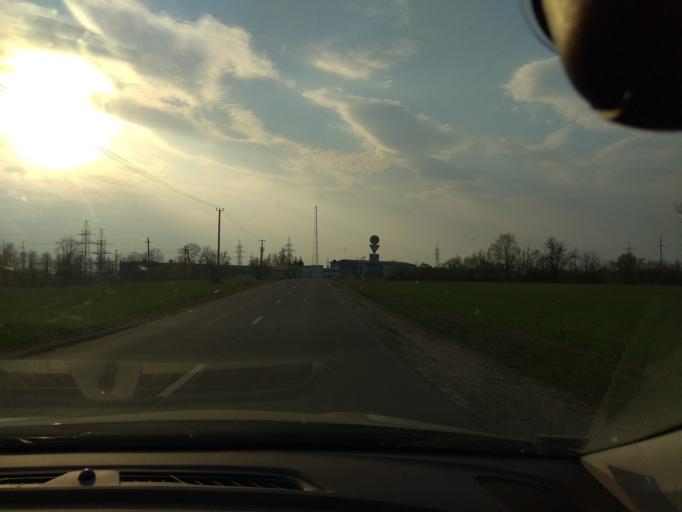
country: LT
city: Baltoji Voke
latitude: 54.6106
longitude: 25.1237
